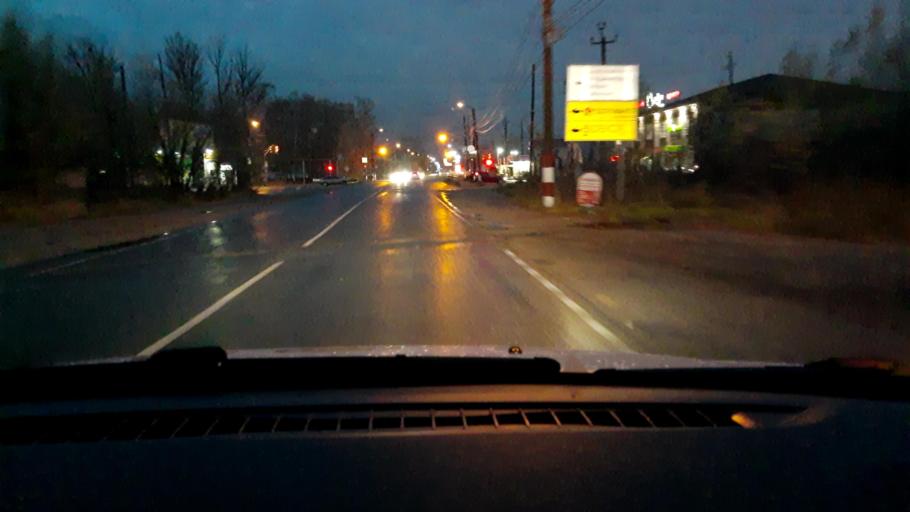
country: RU
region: Nizjnij Novgorod
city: Bor
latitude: 56.3561
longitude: 44.0903
